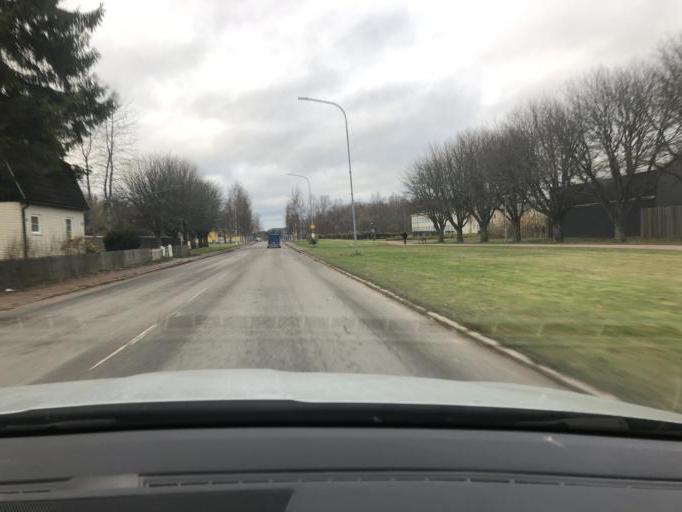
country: SE
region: Uppsala
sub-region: Tierps Kommun
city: Tierp
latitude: 60.3463
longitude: 17.5026
